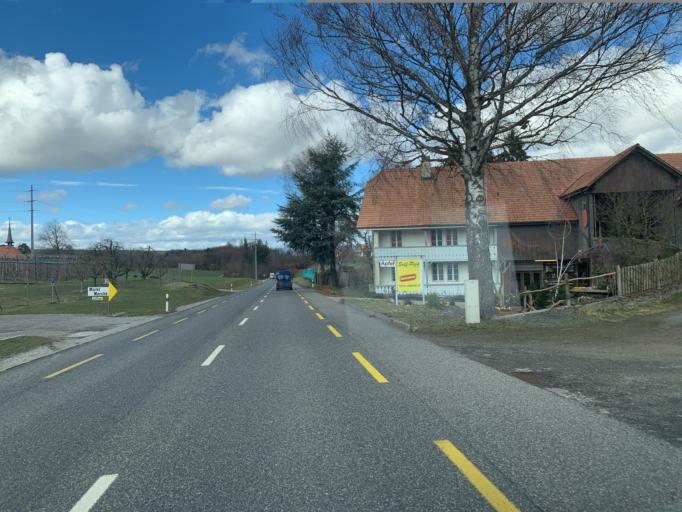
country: CH
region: Fribourg
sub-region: Sense District
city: Dudingen
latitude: 46.8703
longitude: 7.1943
